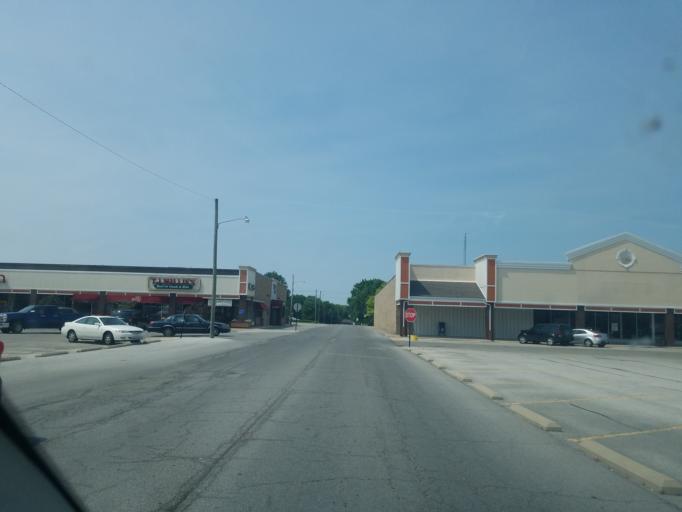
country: US
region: Ohio
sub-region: Seneca County
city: Tiffin
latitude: 41.1124
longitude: -83.2065
